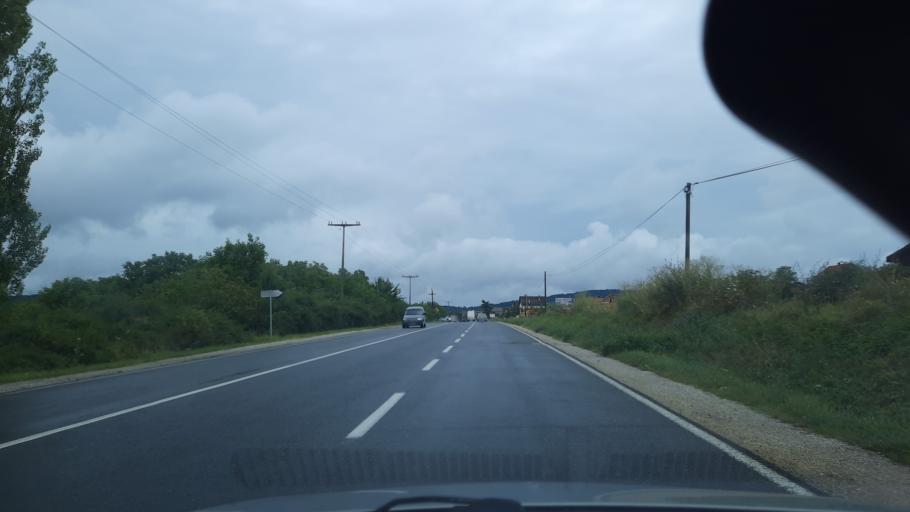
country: RS
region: Central Serbia
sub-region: Sumadijski Okrug
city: Kragujevac
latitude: 43.9839
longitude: 20.8344
